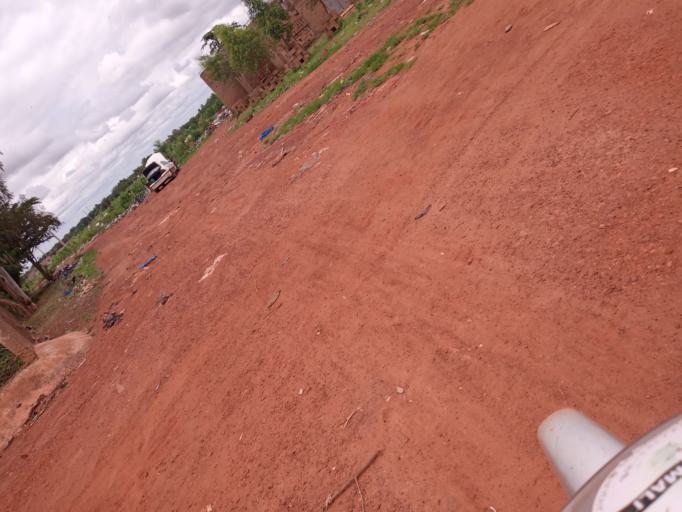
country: ML
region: Bamako
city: Bamako
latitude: 12.5467
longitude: -7.9980
